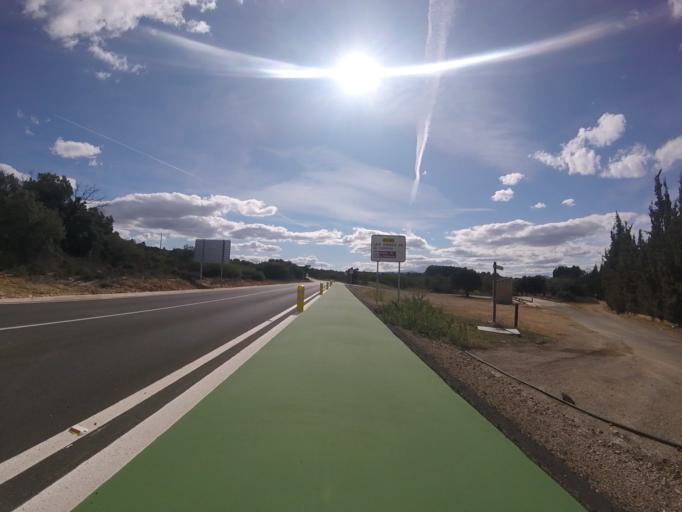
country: ES
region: Valencia
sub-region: Provincia de Castello
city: Cati
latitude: 40.4159
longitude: 0.0712
